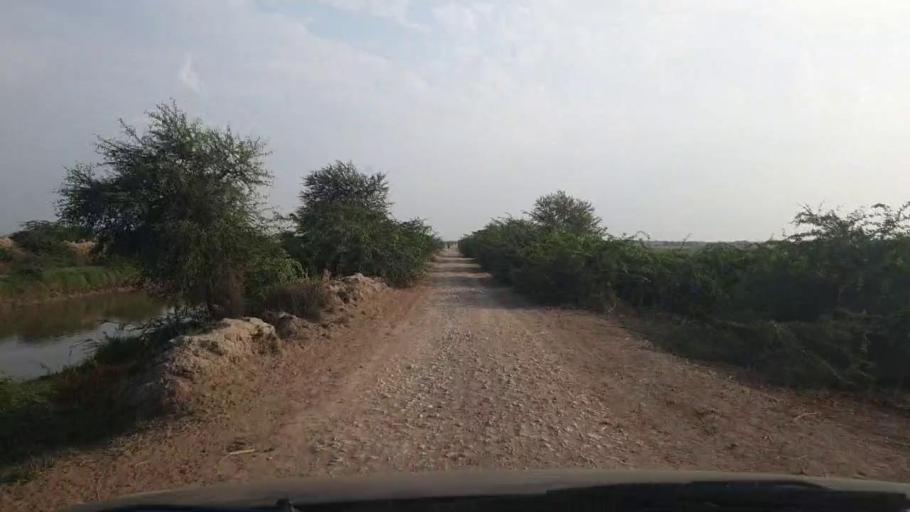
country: PK
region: Sindh
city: Badin
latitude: 24.5645
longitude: 68.6677
